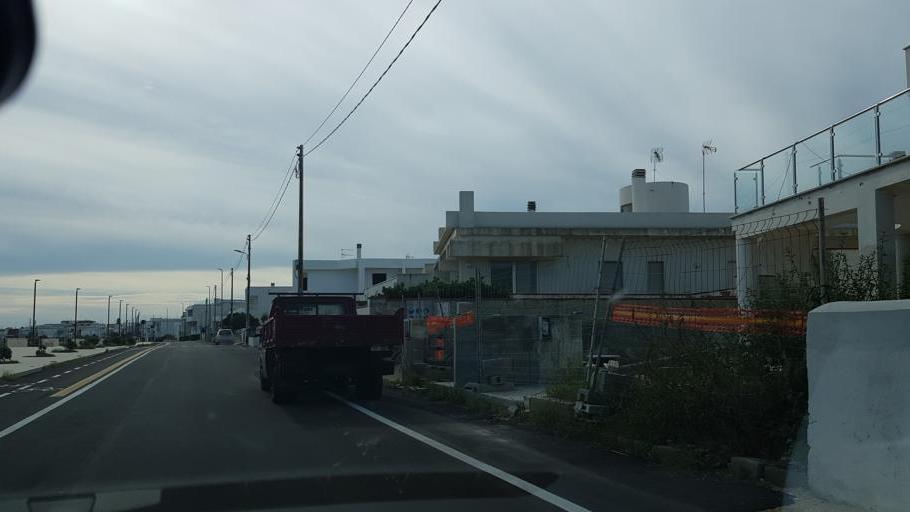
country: IT
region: Apulia
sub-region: Provincia di Lecce
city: Borgagne
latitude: 40.3061
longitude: 18.3979
